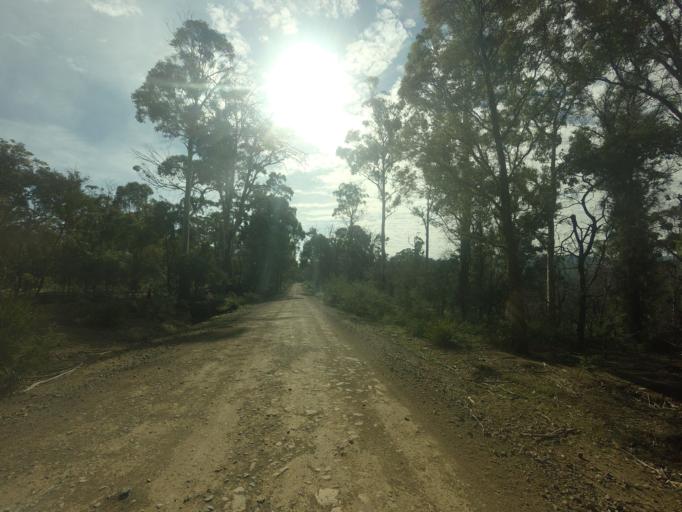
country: AU
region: Tasmania
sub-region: Sorell
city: Sorell
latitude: -42.5476
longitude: 147.4579
